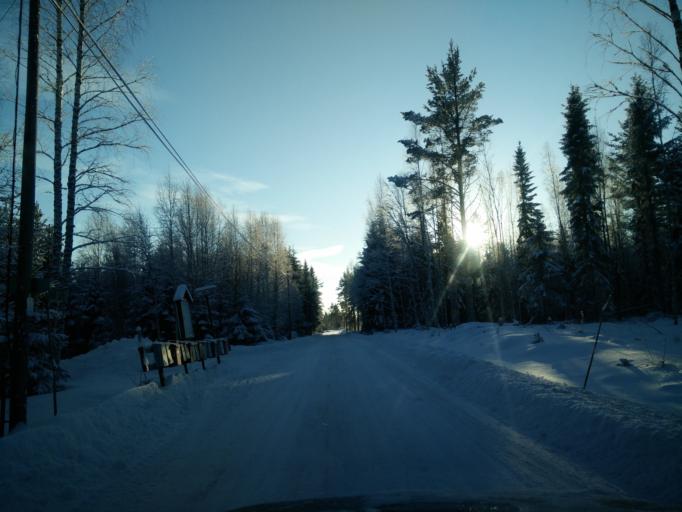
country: SE
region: Vaesternorrland
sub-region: Sundsvalls Kommun
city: Njurundabommen
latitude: 62.2132
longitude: 17.4936
